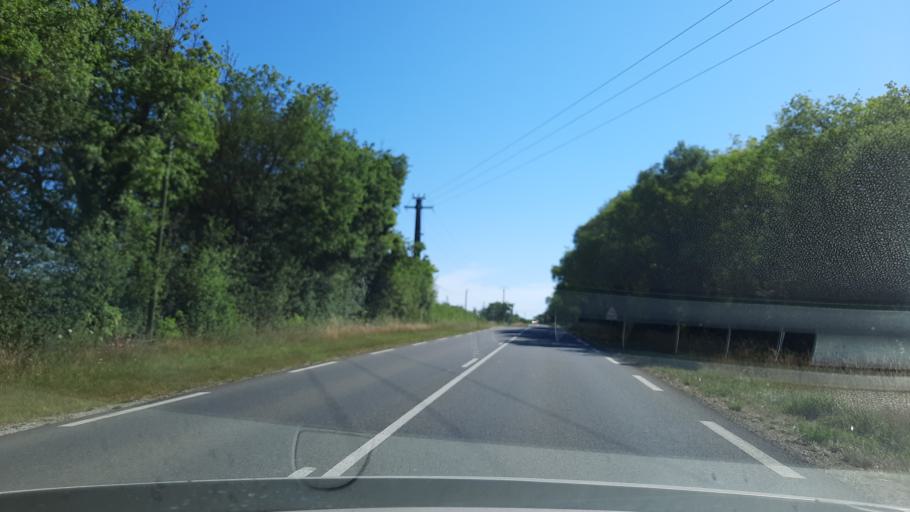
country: FR
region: Midi-Pyrenees
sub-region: Departement du Tarn-et-Garonne
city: Caylus
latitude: 44.2058
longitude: 1.7147
